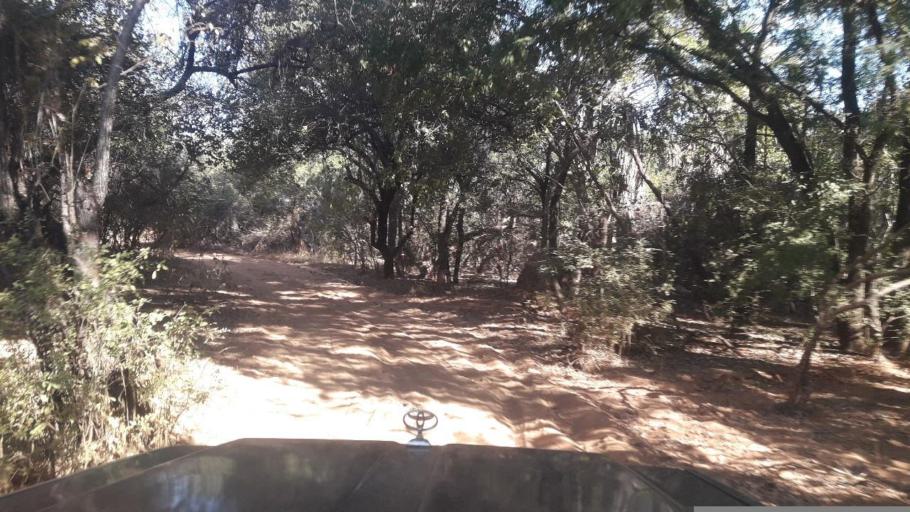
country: MG
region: Boeny
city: Sitampiky
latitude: -16.3941
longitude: 45.5935
